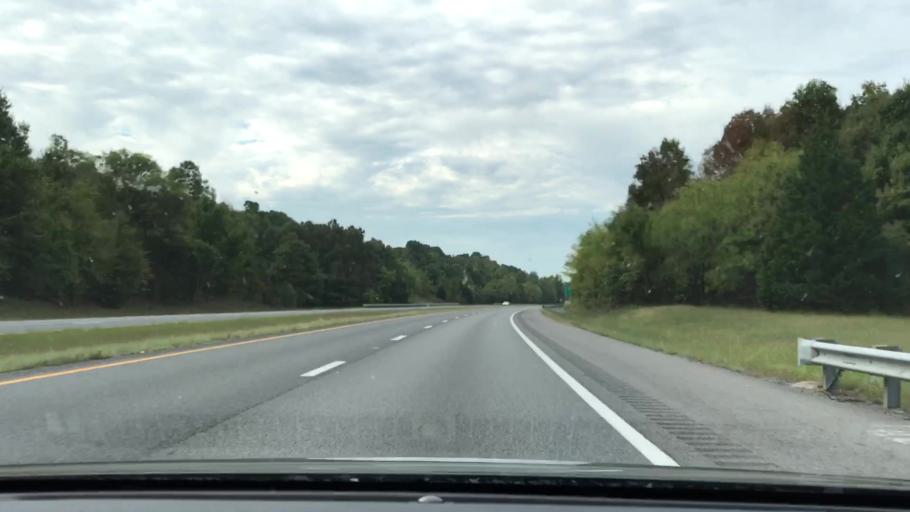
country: US
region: Kentucky
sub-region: Marshall County
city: Benton
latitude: 36.8969
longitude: -88.3482
